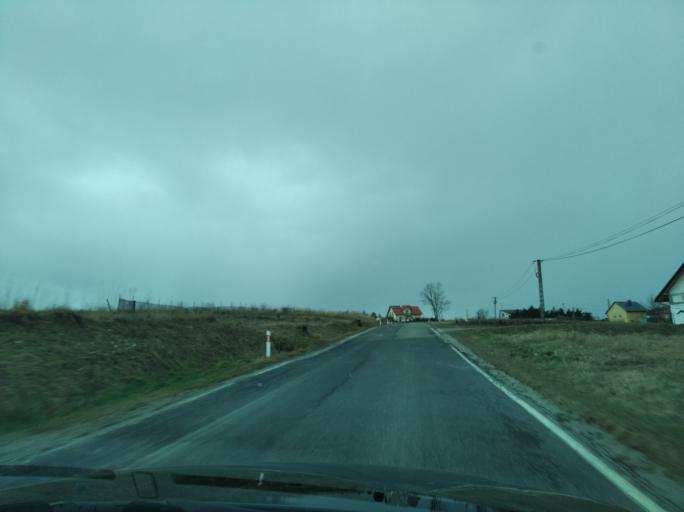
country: PL
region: Subcarpathian Voivodeship
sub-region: Powiat rzeszowski
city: Hyzne
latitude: 49.9183
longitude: 22.1973
